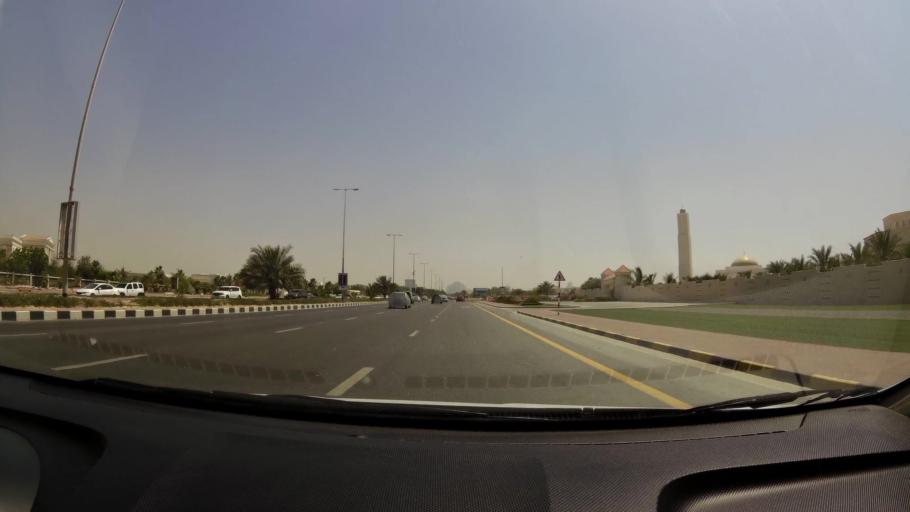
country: AE
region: Ajman
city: Ajman
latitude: 25.4161
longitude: 55.4869
